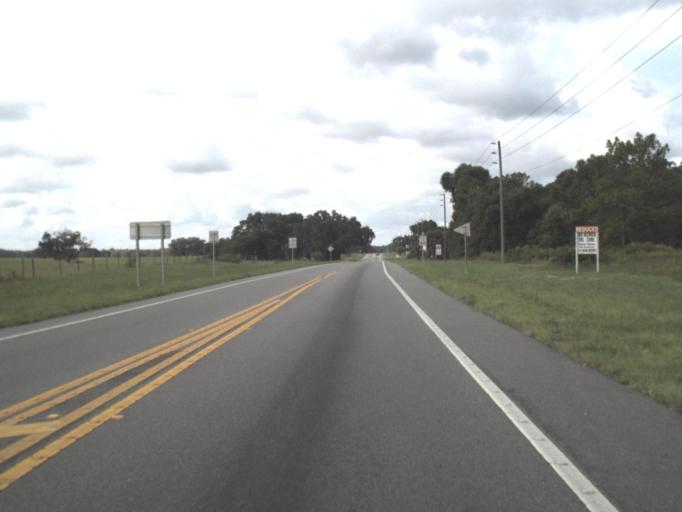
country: US
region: Florida
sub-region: Hernando County
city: Ridge Manor
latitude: 28.5054
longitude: -82.1710
